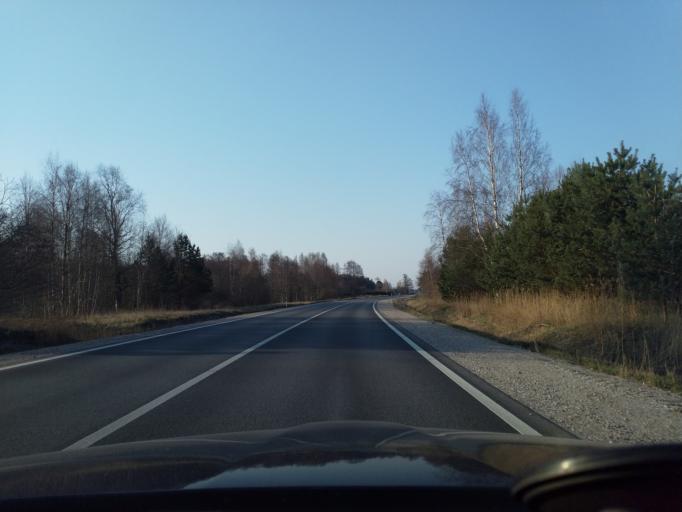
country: LV
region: Liepaja
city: Liepaja
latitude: 56.4236
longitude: 21.0075
